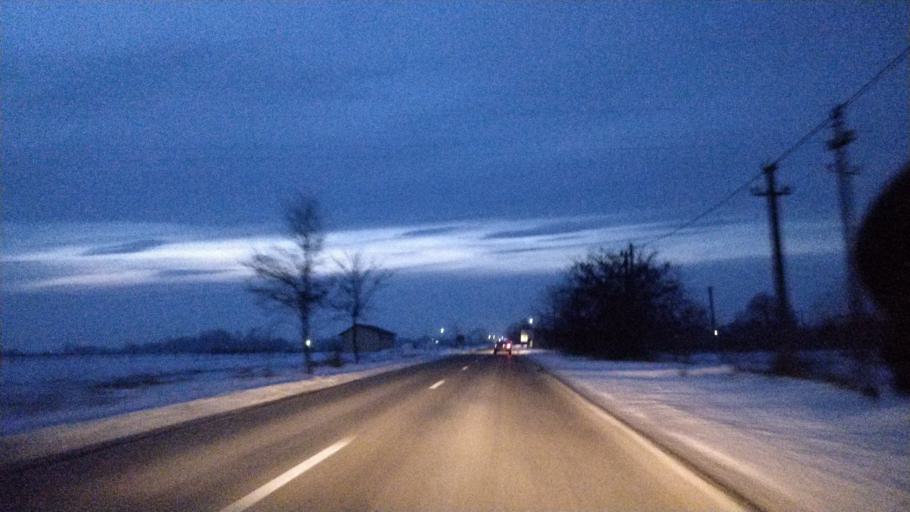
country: RO
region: Vrancea
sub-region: Comuna Rastoaca
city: Rastoaca
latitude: 45.6543
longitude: 27.3009
